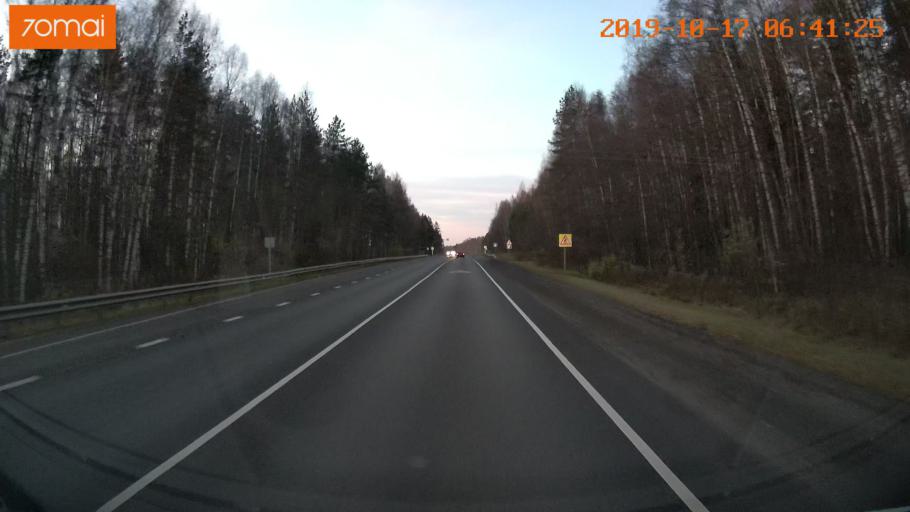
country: RU
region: Ivanovo
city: Nerl'
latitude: 56.6154
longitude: 40.5604
